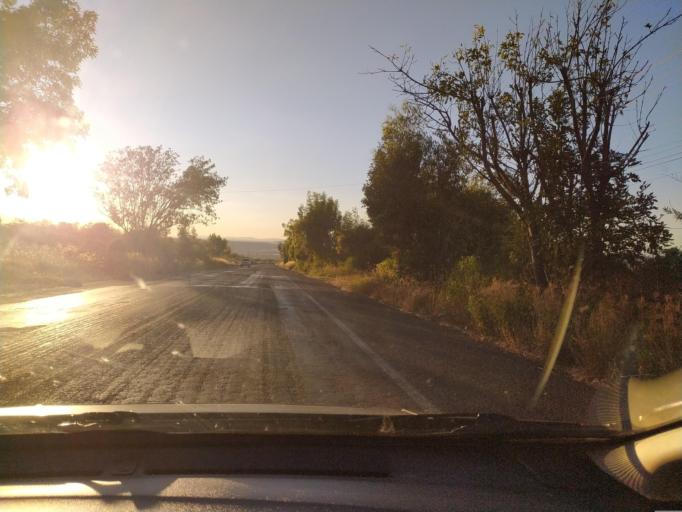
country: MX
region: Jalisco
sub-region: San Julian
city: Colonia Veintitres de Mayo
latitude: 21.0090
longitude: -102.2525
